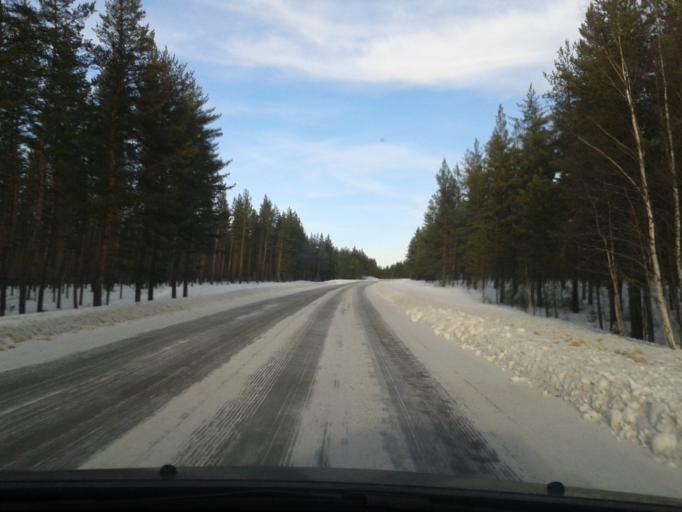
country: SE
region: Vaesternorrland
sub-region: OErnskoeldsviks Kommun
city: Bredbyn
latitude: 63.6113
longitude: 17.9014
